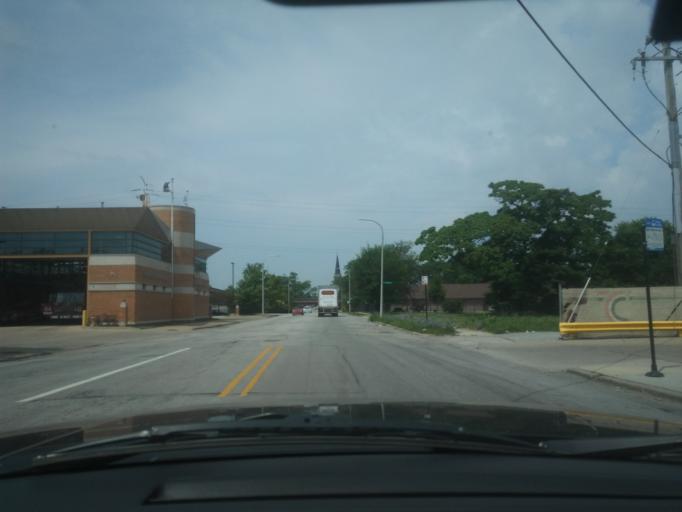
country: US
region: Illinois
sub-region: Cook County
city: Chicago
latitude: 41.7874
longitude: -87.6258
